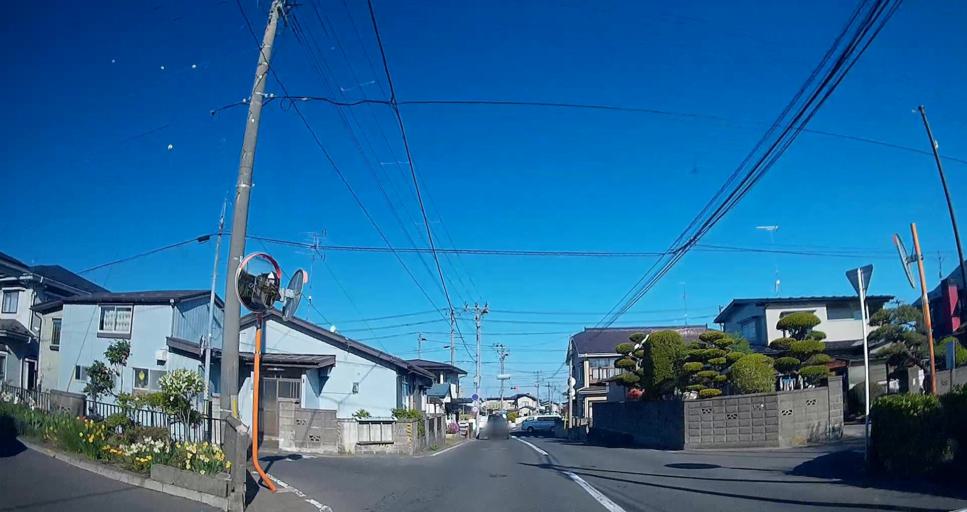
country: JP
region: Aomori
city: Hachinohe
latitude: 40.5247
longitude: 141.5512
